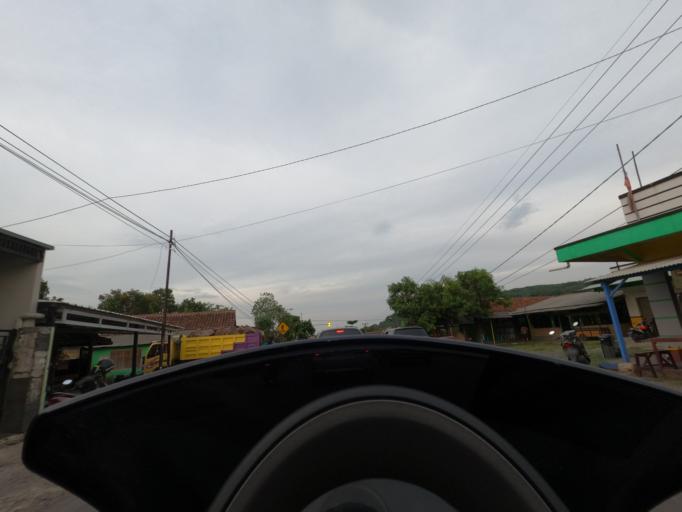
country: ID
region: West Java
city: Lembang
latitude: -6.6542
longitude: 107.7173
